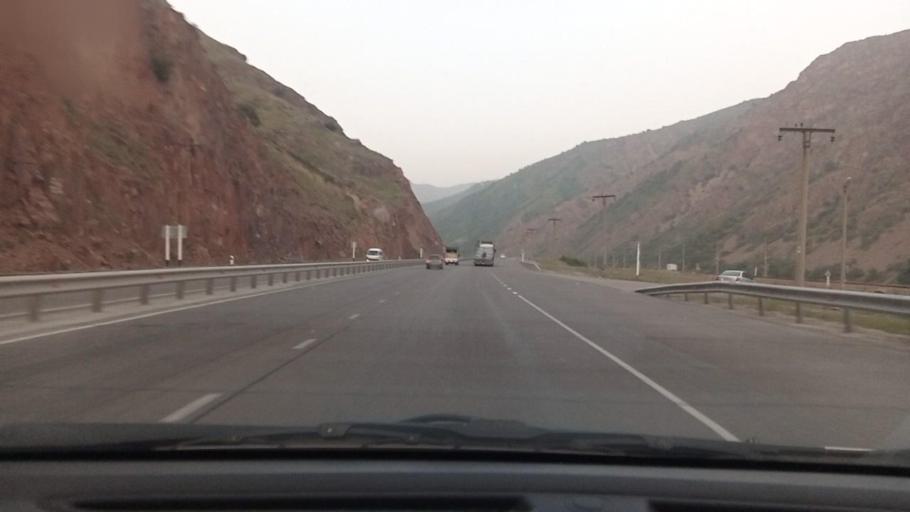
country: UZ
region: Toshkent
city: Angren
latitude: 41.1405
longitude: 70.3879
